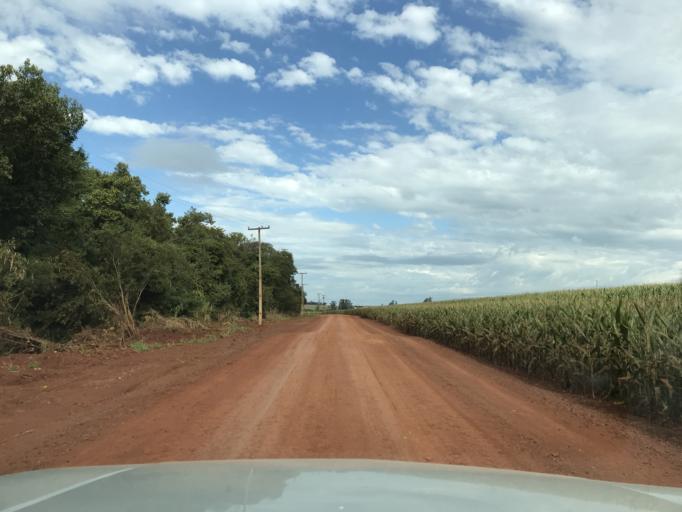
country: BR
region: Parana
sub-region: Palotina
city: Palotina
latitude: -24.3131
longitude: -53.8077
